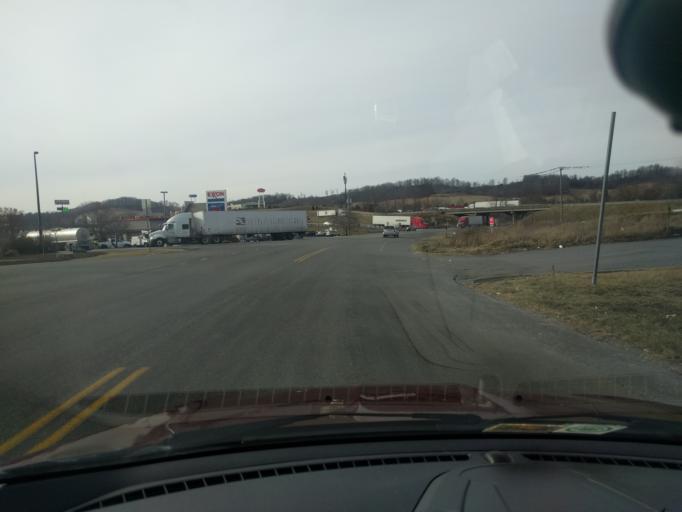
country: US
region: Virginia
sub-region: Augusta County
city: Stuarts Draft
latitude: 37.9308
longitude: -79.2265
